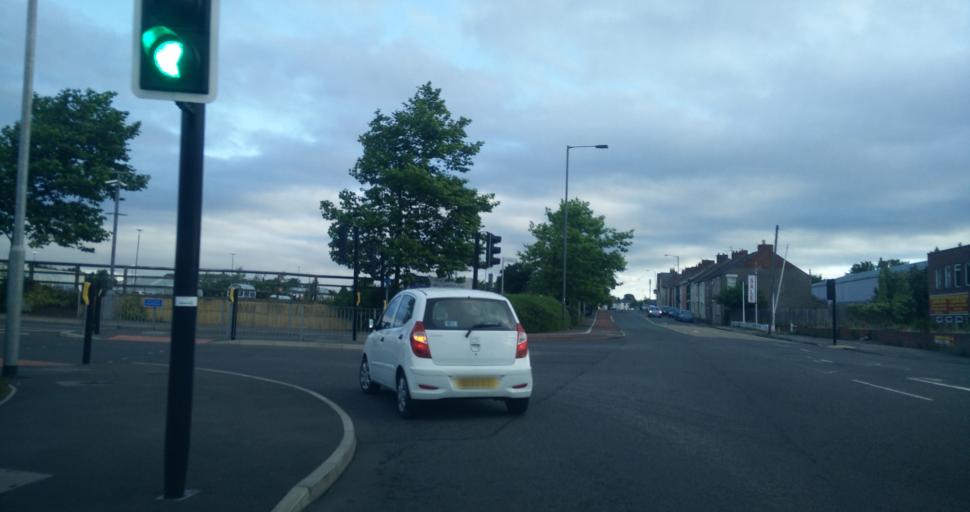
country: GB
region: England
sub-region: County Durham
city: Durham
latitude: 54.7776
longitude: -1.5399
